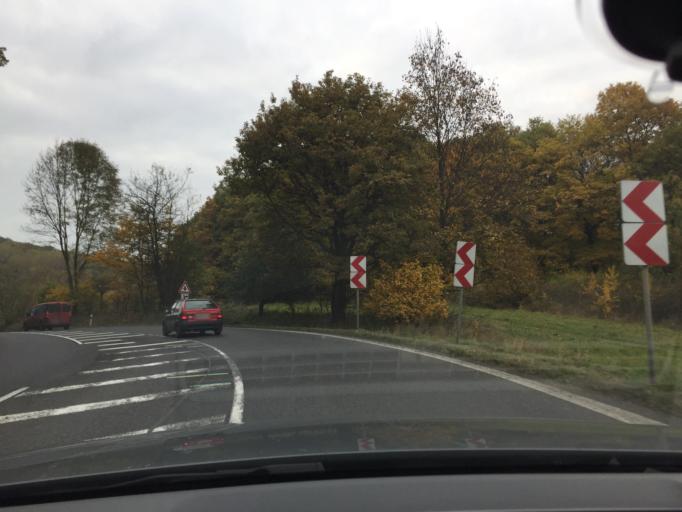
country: CZ
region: Ustecky
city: Rehlovice
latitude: 50.5722
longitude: 13.9410
